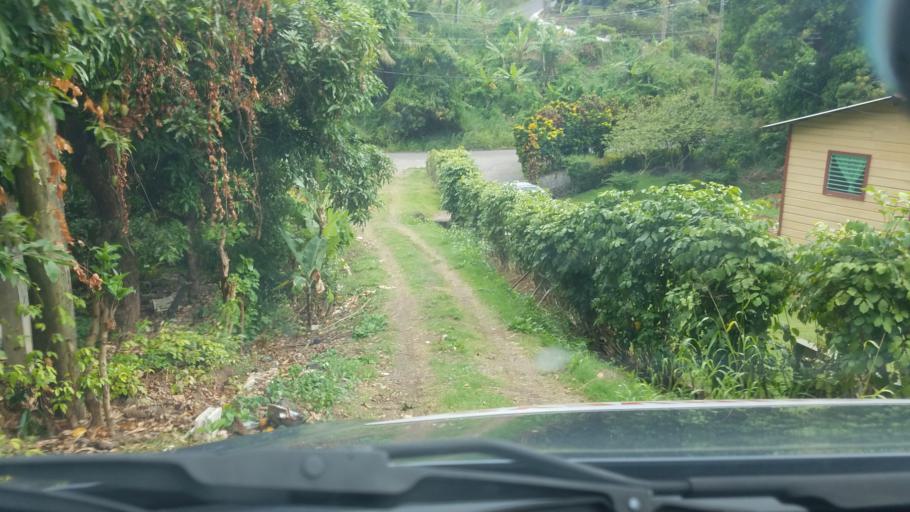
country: LC
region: Gros-Islet
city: Gros Islet
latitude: 14.0599
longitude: -60.9491
